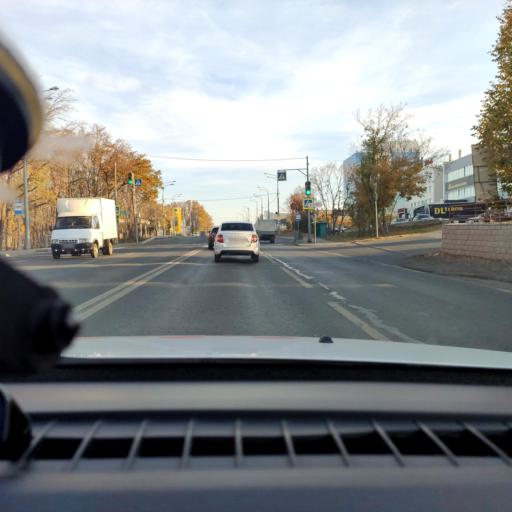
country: RU
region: Samara
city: Samara
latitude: 53.2728
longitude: 50.2250
